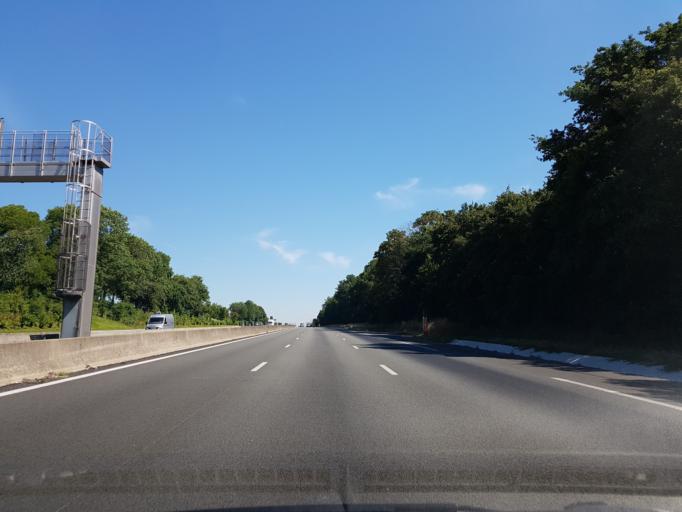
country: FR
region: Picardie
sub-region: Departement de l'Oise
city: Longueil-Sainte-Marie
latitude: 49.3524
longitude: 2.7016
